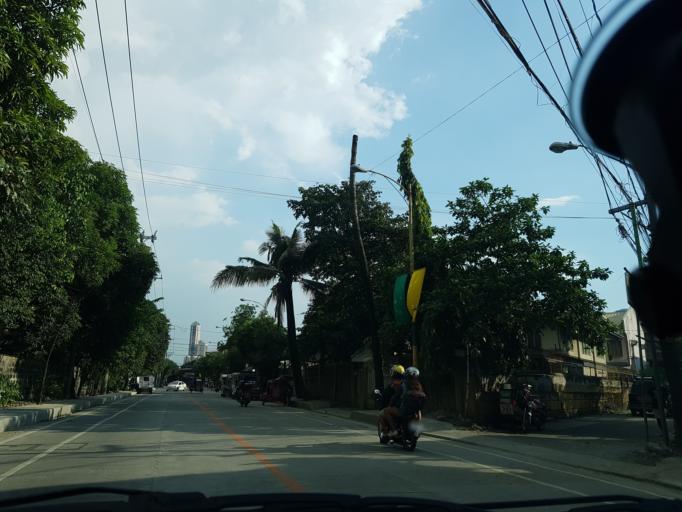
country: PH
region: Metro Manila
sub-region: Marikina
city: Calumpang
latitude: 14.6143
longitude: 121.0869
